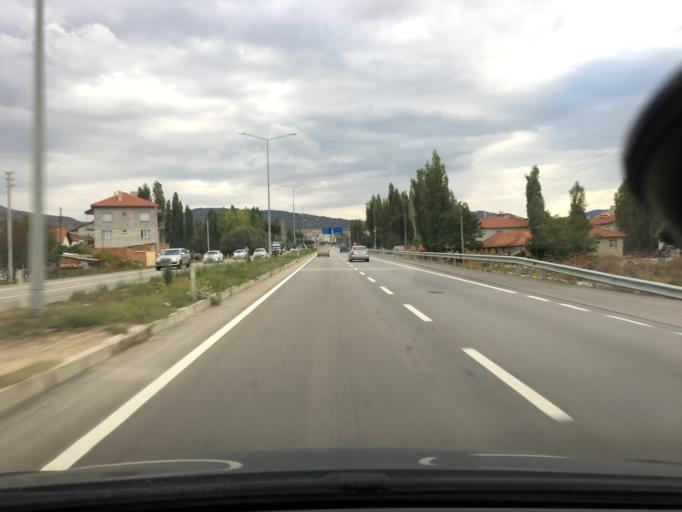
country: TR
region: Afyonkarahisar
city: Sincanli
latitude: 38.7346
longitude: 30.3484
